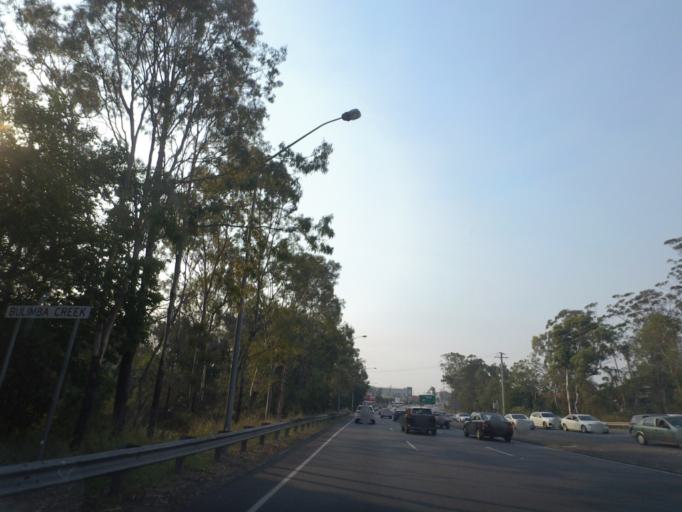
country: AU
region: Queensland
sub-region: Brisbane
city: Upper Mount Gravatt
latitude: -27.5684
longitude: 153.0893
